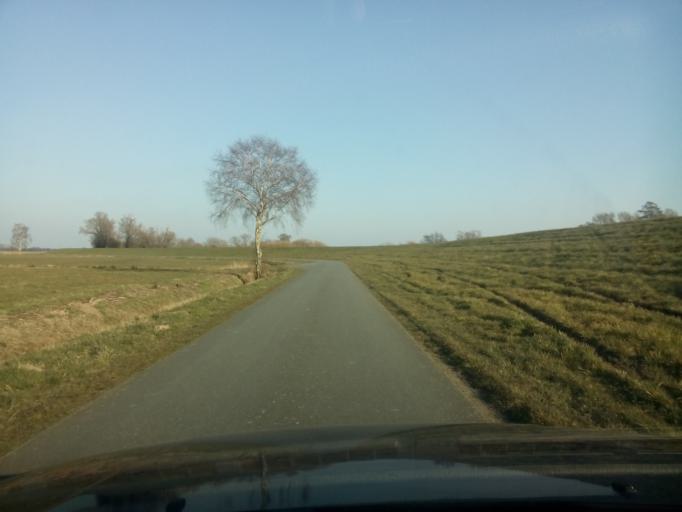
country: DE
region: Lower Saxony
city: Osterholz-Scharmbeck
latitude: 53.1641
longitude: 8.8238
